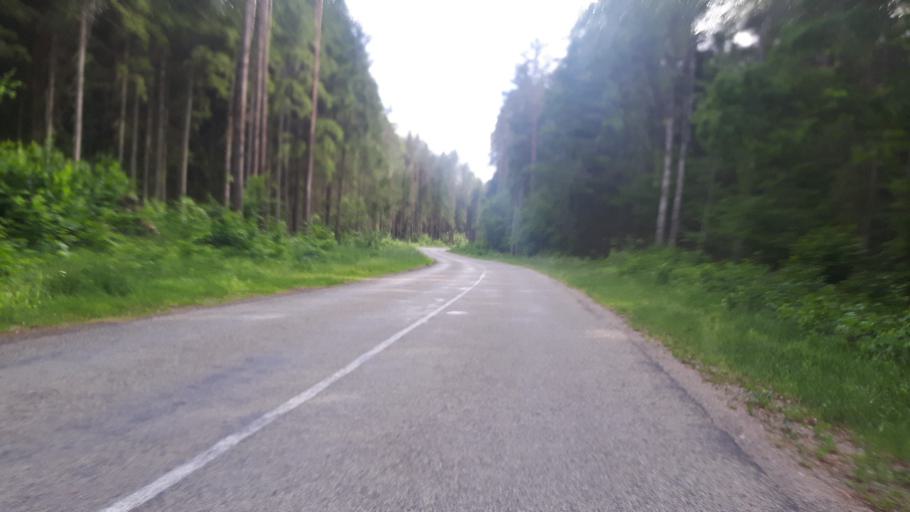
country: LV
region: Engure
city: Smarde
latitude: 56.9970
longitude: 23.3210
